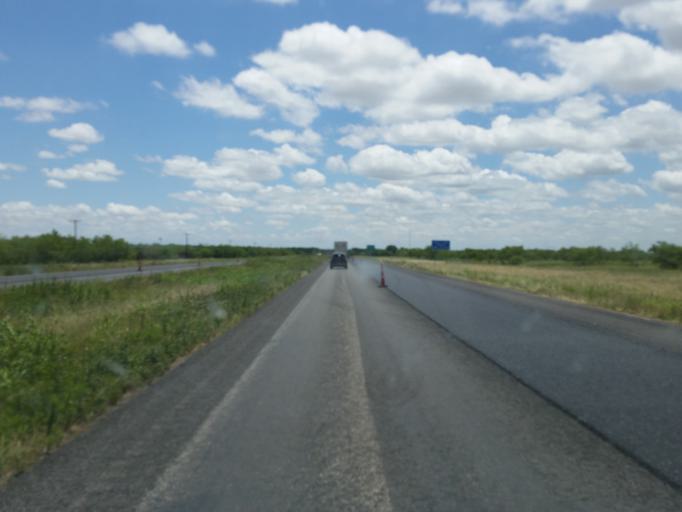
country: US
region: Texas
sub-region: Scurry County
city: Snyder
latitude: 32.7692
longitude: -100.9374
